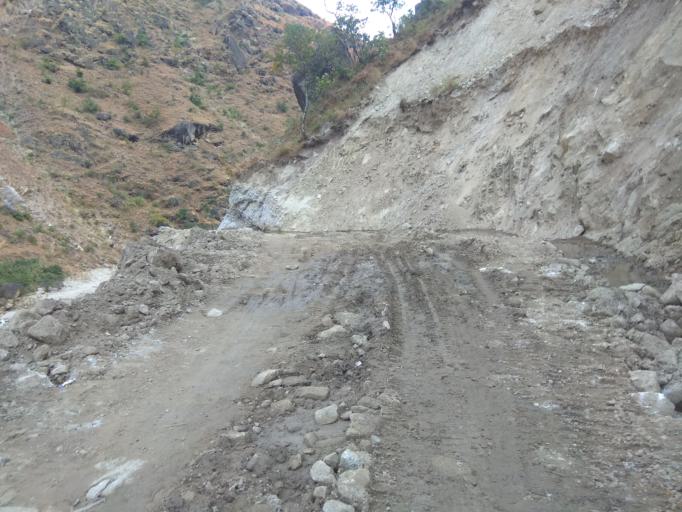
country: NP
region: Far Western
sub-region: Seti Zone
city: Achham
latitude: 29.2286
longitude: 81.6206
